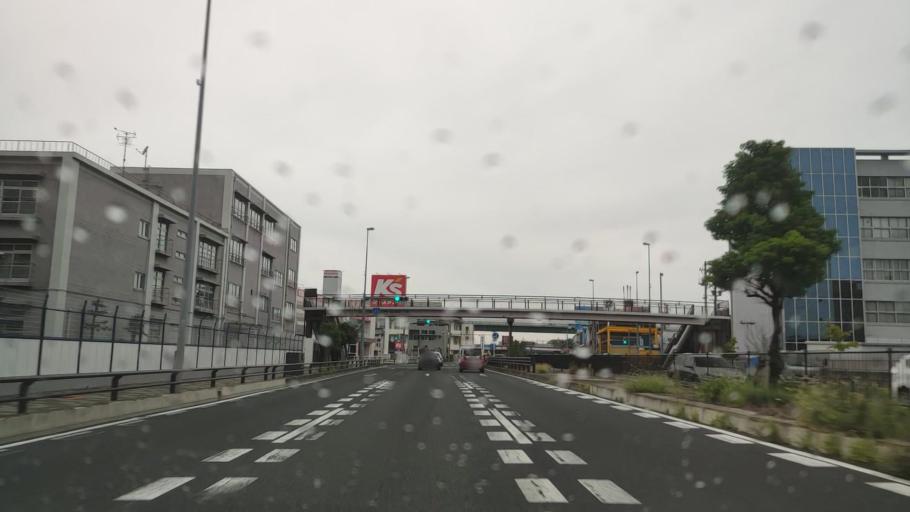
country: JP
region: Aichi
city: Nagoya-shi
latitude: 35.2000
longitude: 136.8814
